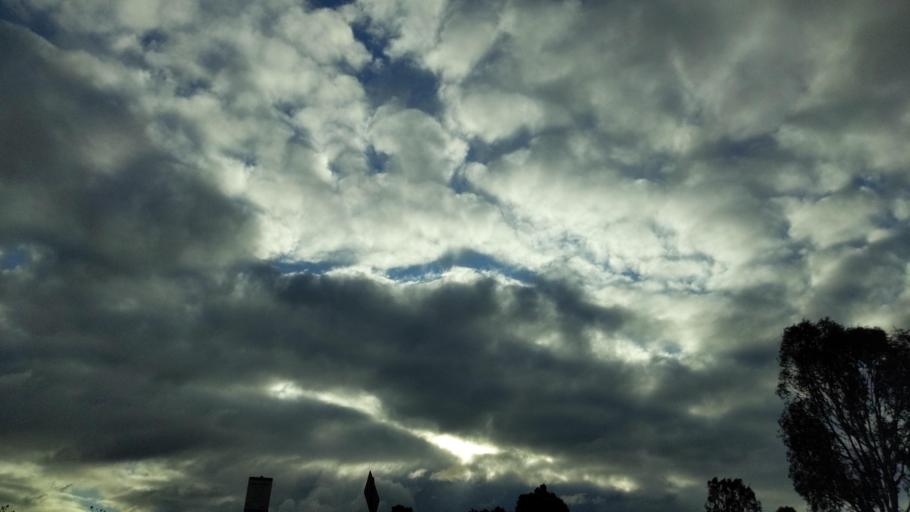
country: AU
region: New South Wales
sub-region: Wagga Wagga
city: Wagga Wagga
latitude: -35.0696
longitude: 147.3799
